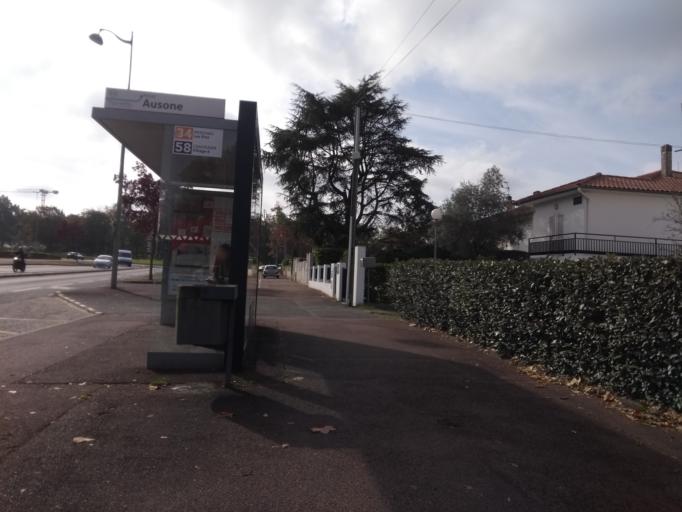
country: FR
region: Aquitaine
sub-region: Departement de la Gironde
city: Talence
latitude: 44.8014
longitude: -0.6171
